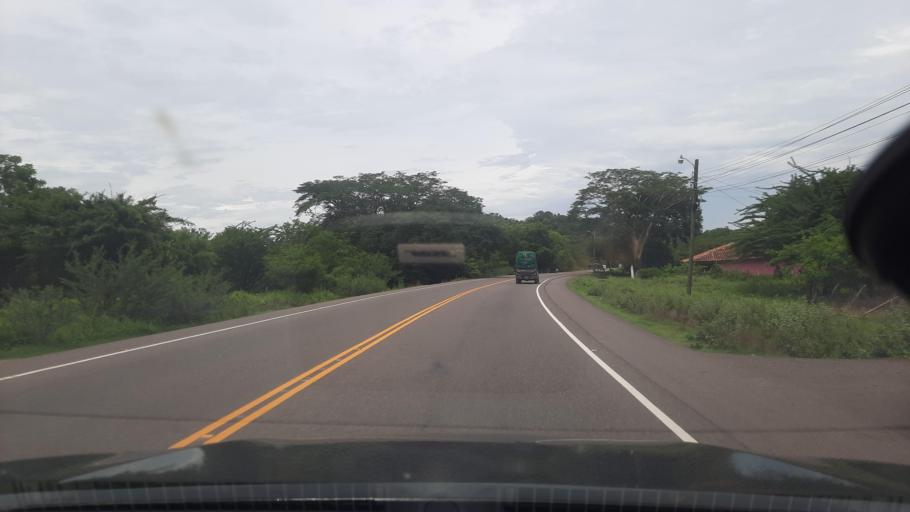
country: HN
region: Valle
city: Goascoran
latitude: 13.5627
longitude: -87.6631
